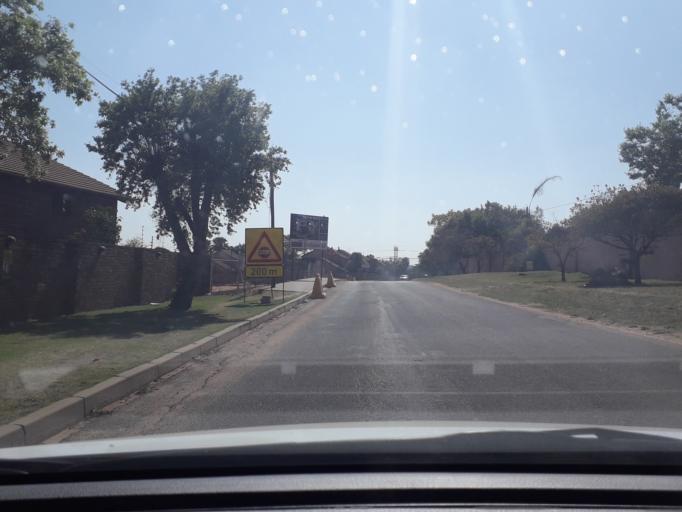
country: ZA
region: Gauteng
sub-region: City of Johannesburg Metropolitan Municipality
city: Roodepoort
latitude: -26.0822
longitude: 27.9620
